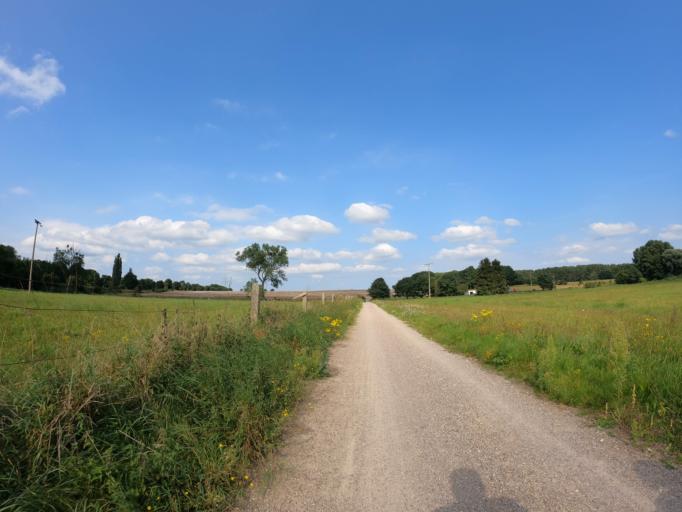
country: DE
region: Mecklenburg-Vorpommern
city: Malchow
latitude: 53.5033
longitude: 12.4295
